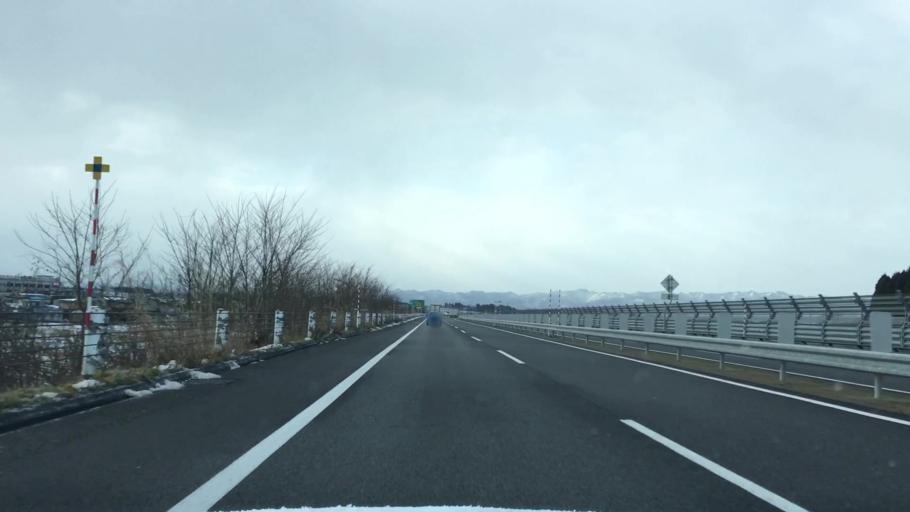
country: JP
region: Akita
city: Odate
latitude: 40.2963
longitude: 140.5540
